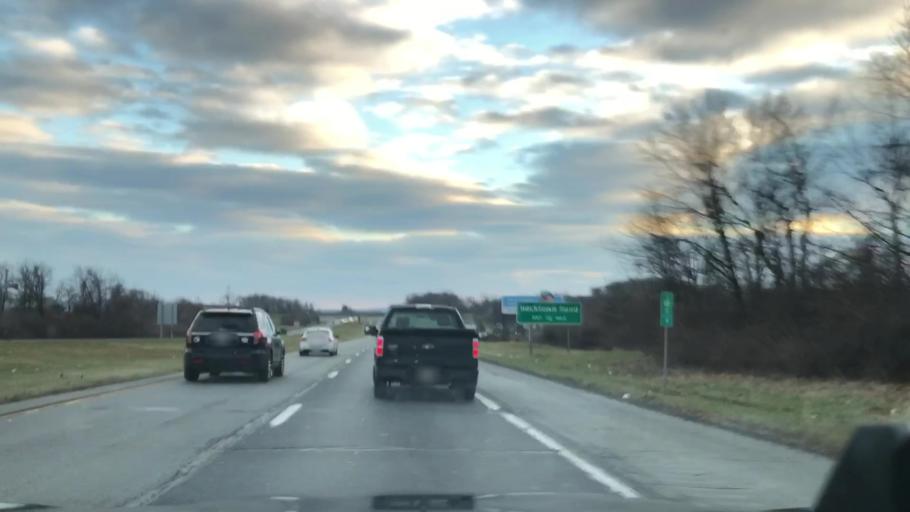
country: US
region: Pennsylvania
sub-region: Northampton County
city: Palmer Heights
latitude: 40.7095
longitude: -75.2903
